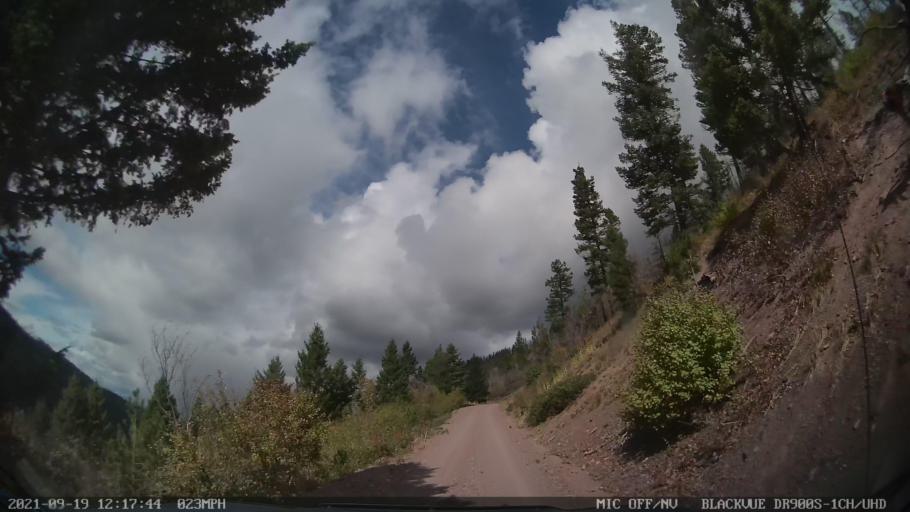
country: US
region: Montana
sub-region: Missoula County
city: Seeley Lake
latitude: 47.1726
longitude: -113.3609
